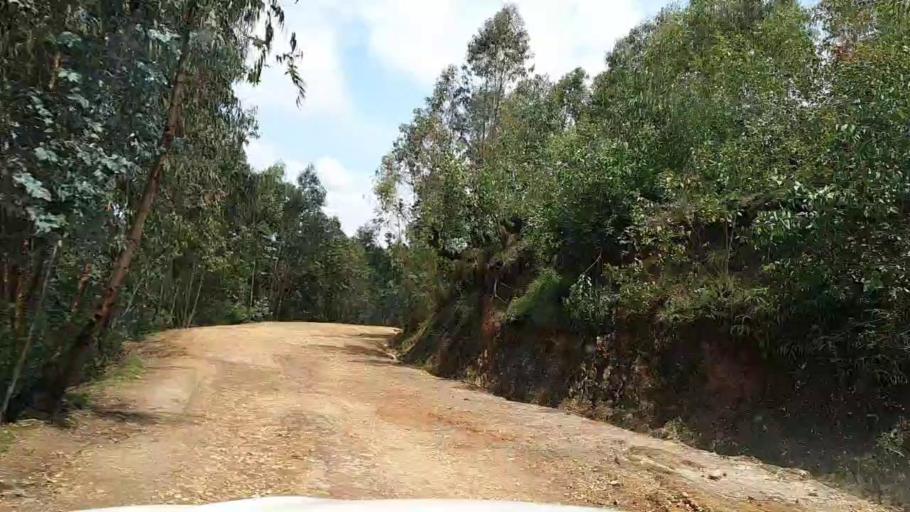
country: RW
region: Southern Province
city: Gikongoro
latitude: -2.3388
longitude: 29.5136
